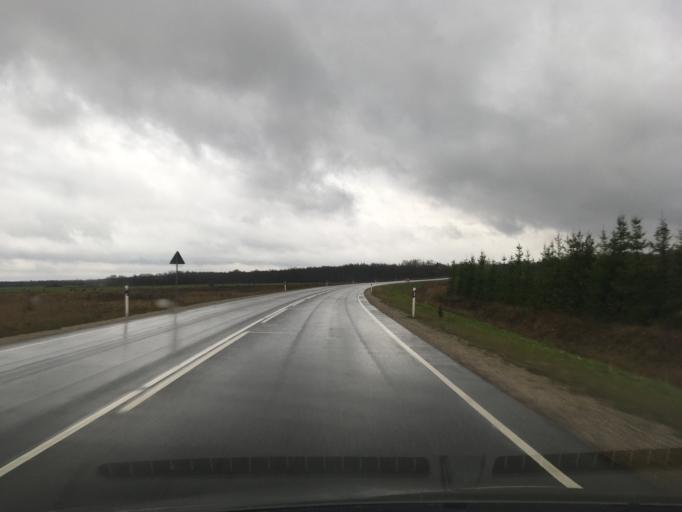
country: EE
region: Laeaene
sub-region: Lihula vald
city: Lihula
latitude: 58.7403
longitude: 23.9972
